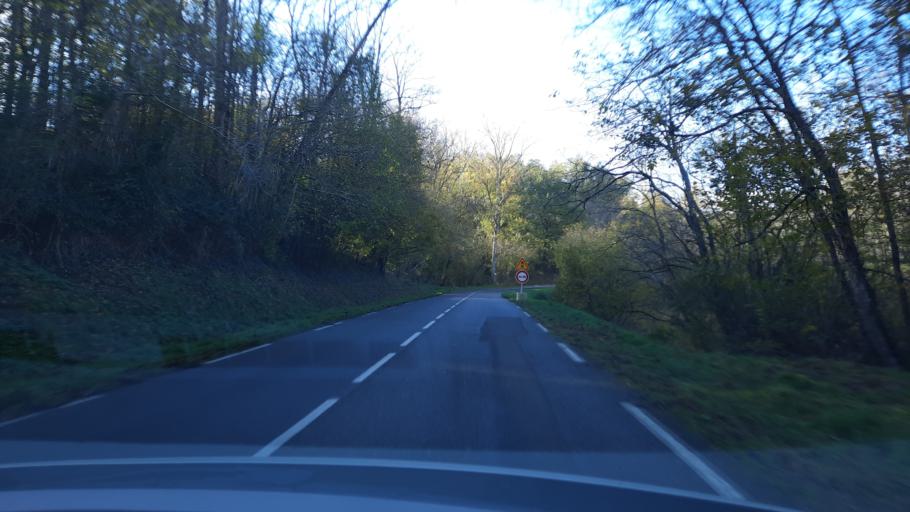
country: FR
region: Midi-Pyrenees
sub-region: Departement du Tarn-et-Garonne
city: Molieres
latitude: 44.1208
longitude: 1.3532
